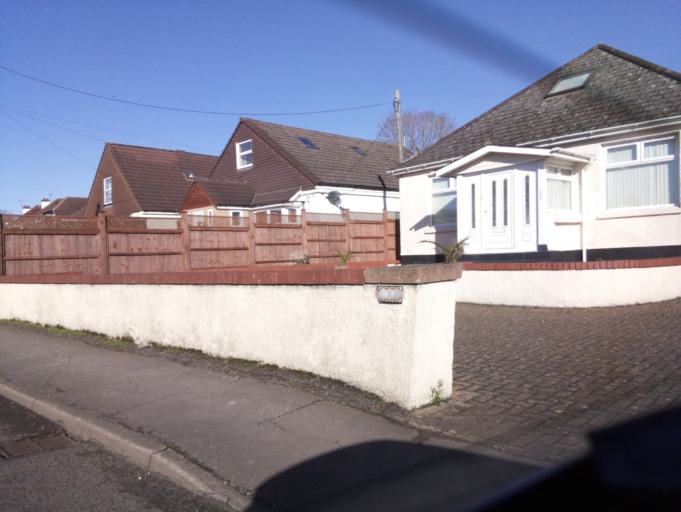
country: GB
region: England
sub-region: Somerset
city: Yeovil
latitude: 50.9534
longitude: -2.6461
